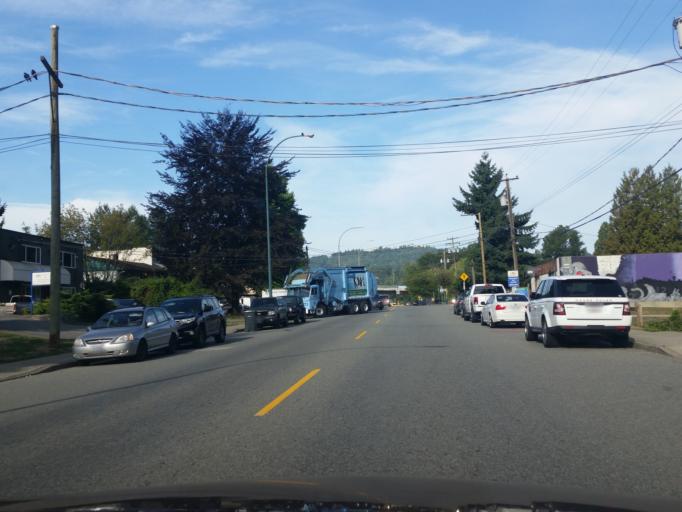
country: CA
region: British Columbia
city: Port Moody
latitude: 49.2789
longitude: -122.8462
